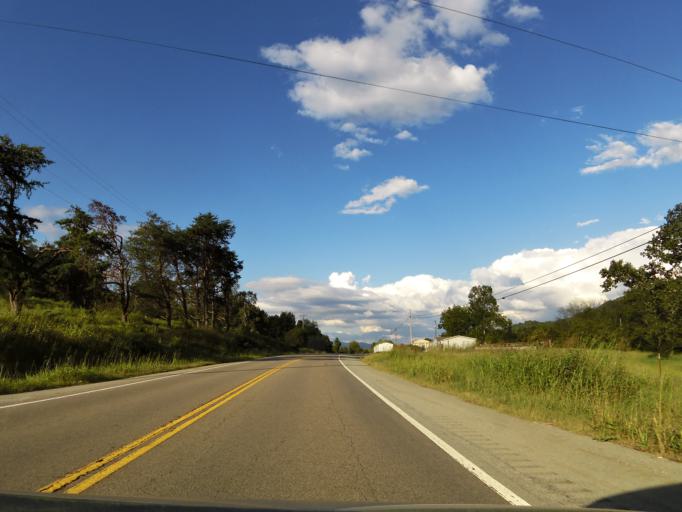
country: US
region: Tennessee
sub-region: Grainger County
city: Blaine
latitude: 36.2250
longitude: -83.6344
